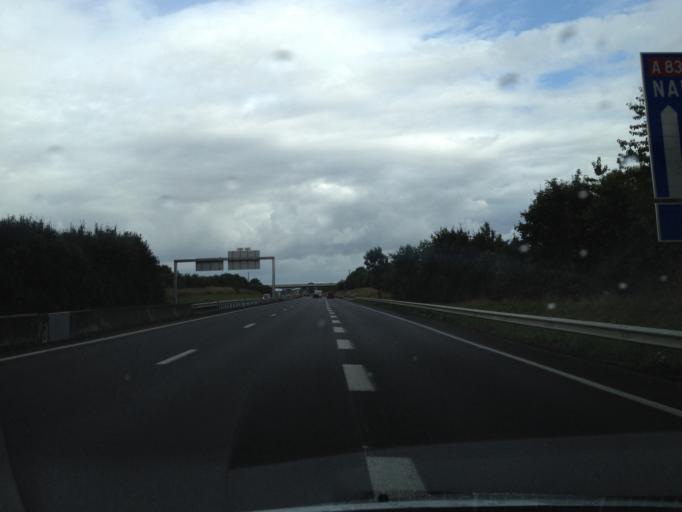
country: FR
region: Pays de la Loire
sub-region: Departement de la Vendee
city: Les Essarts
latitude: 46.7942
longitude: -1.1996
